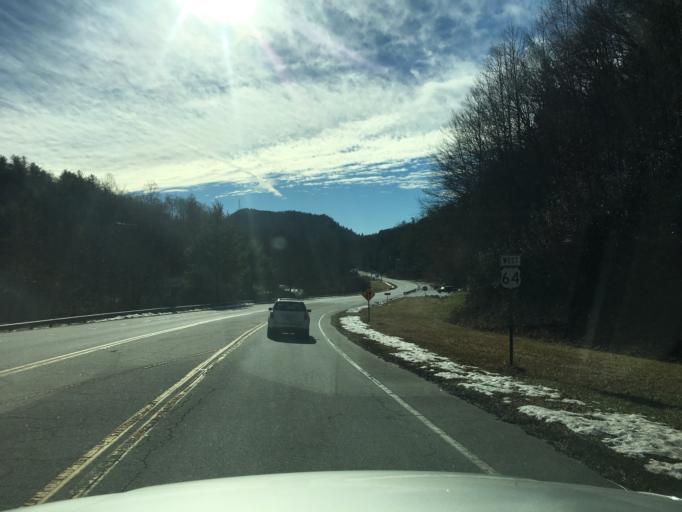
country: US
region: North Carolina
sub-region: Transylvania County
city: Brevard
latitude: 35.1490
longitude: -82.8316
